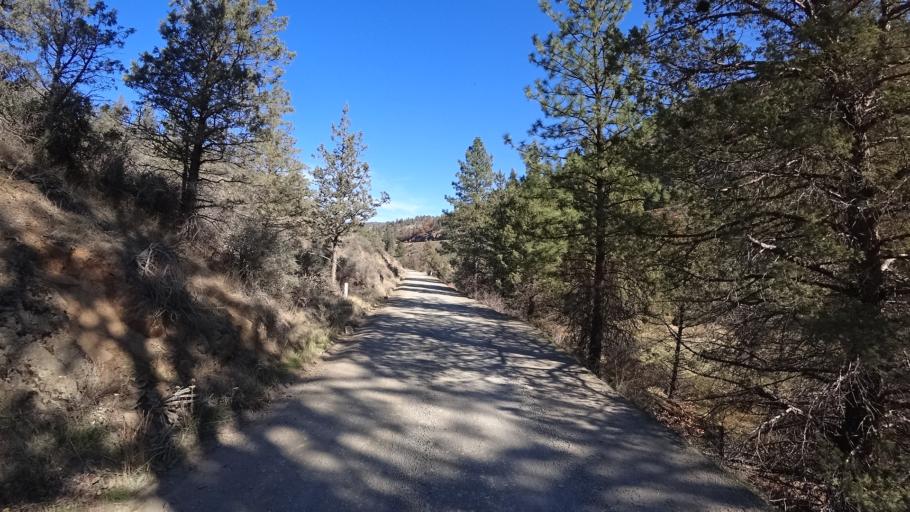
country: US
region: California
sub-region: Siskiyou County
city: Yreka
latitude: 41.7948
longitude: -122.6081
